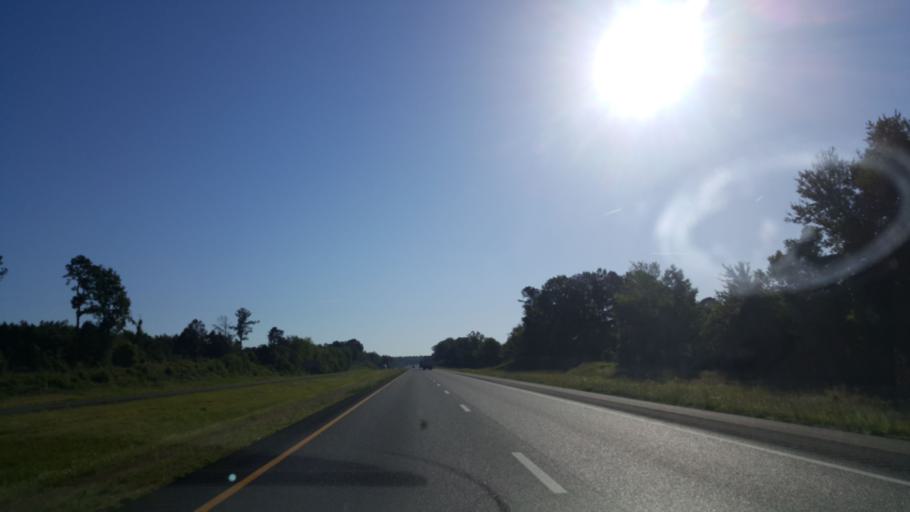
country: US
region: Tennessee
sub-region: Humphreys County
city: New Johnsonville
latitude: 35.8577
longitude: -88.0538
